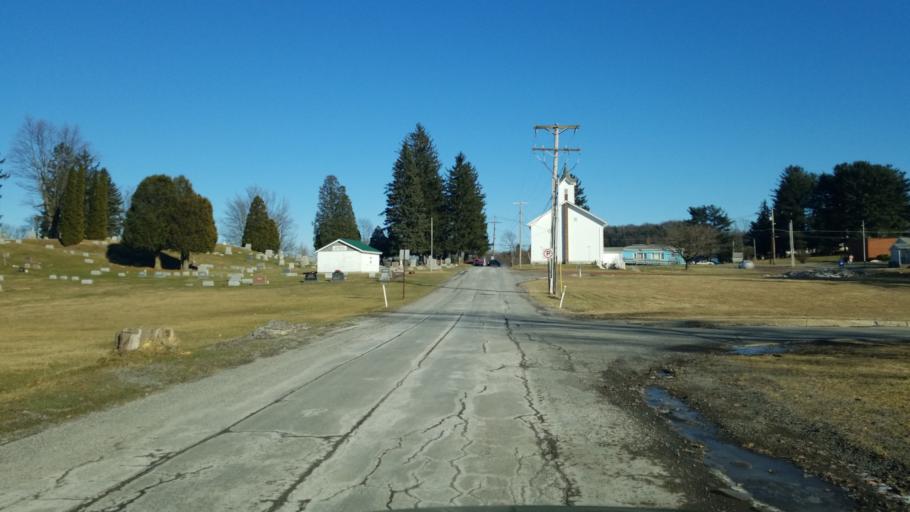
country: US
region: Pennsylvania
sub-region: Clearfield County
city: Sandy
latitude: 41.0539
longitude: -78.7249
